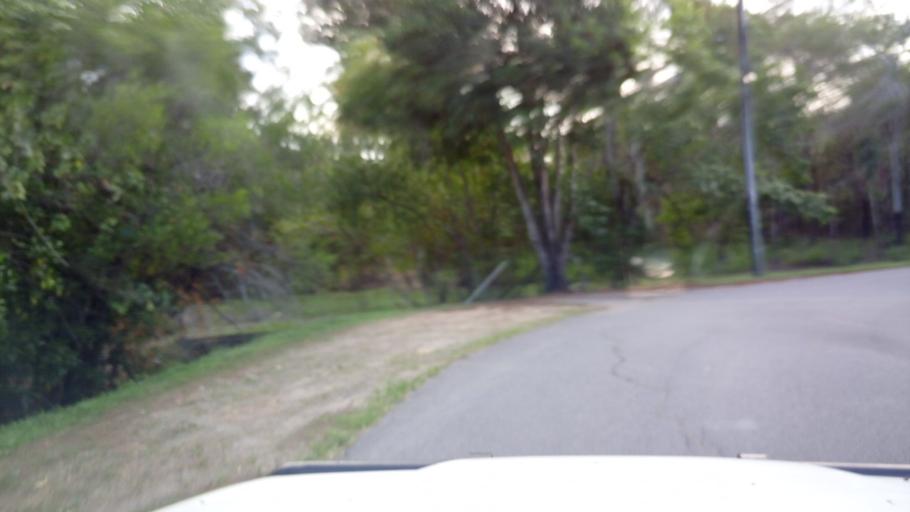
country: AU
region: Queensland
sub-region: Cairns
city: Cairns
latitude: -16.9175
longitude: 145.7555
